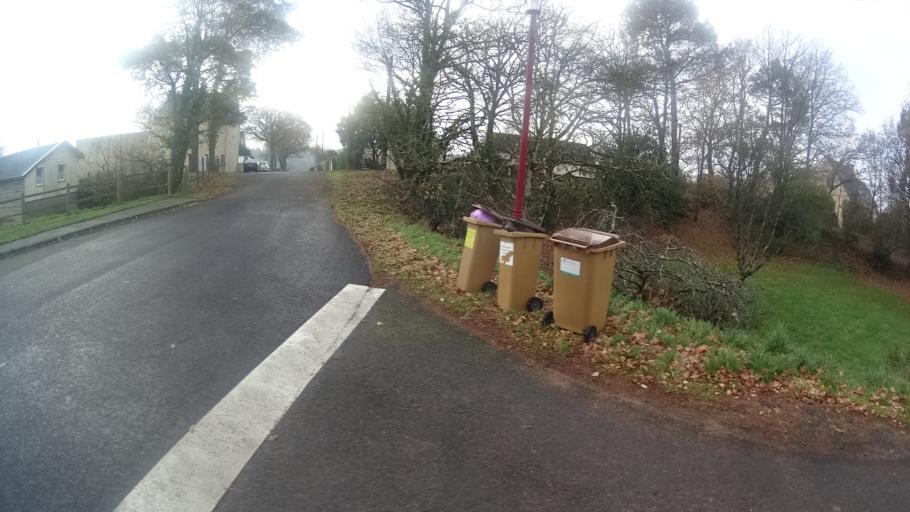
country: FR
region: Pays de la Loire
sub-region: Departement de la Loire-Atlantique
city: Avessac
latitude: 47.6507
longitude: -1.9888
